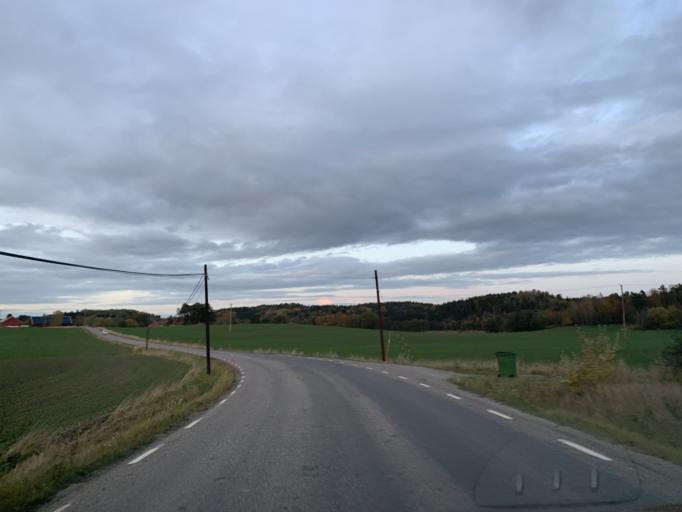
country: SE
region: Stockholm
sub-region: Nynashamns Kommun
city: Osmo
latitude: 58.9511
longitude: 17.7664
